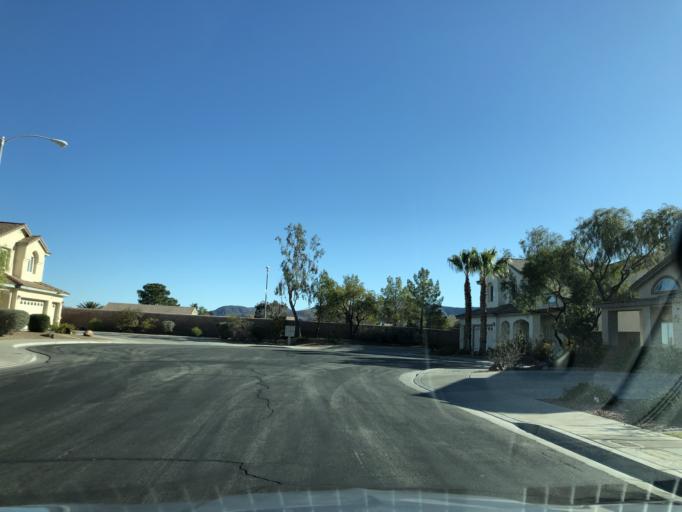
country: US
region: Nevada
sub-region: Clark County
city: Whitney
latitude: 36.0089
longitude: -115.0840
